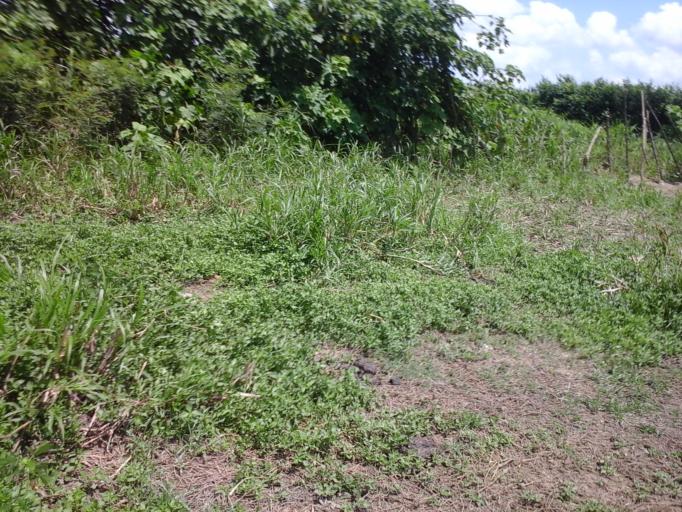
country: CO
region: Bolivar
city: Mahates
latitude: 10.1649
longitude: -75.2747
